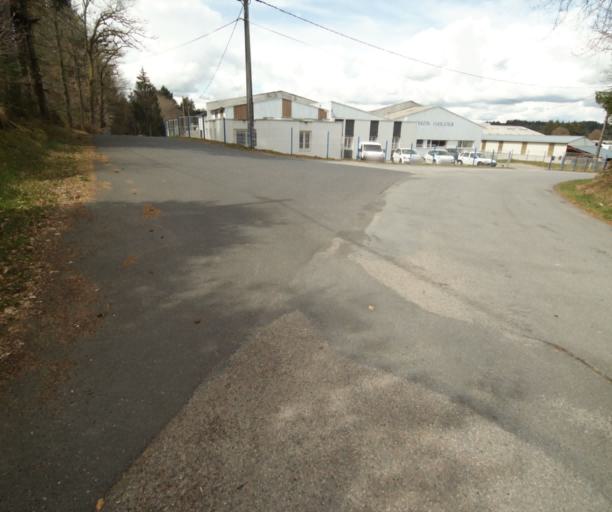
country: FR
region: Limousin
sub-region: Departement de la Correze
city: Correze
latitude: 45.3416
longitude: 1.9473
